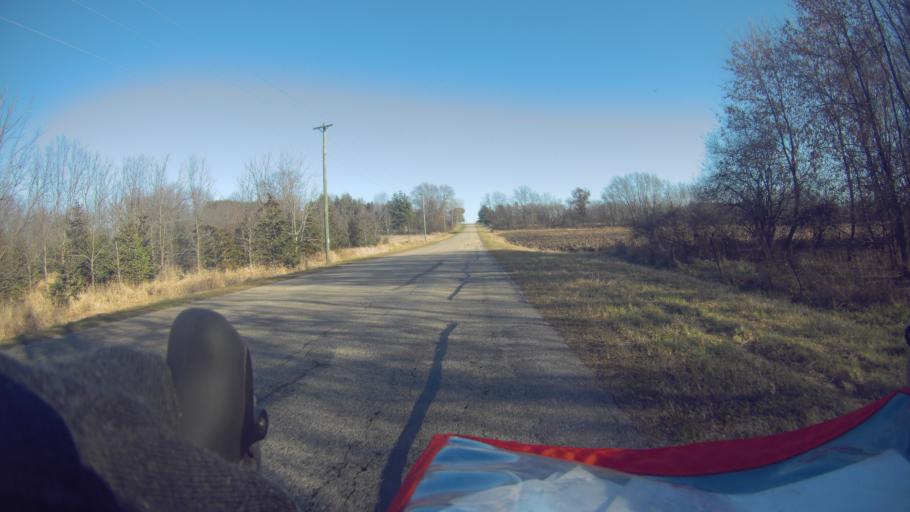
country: US
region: Wisconsin
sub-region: Dane County
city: Stoughton
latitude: 42.8824
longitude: -89.2019
